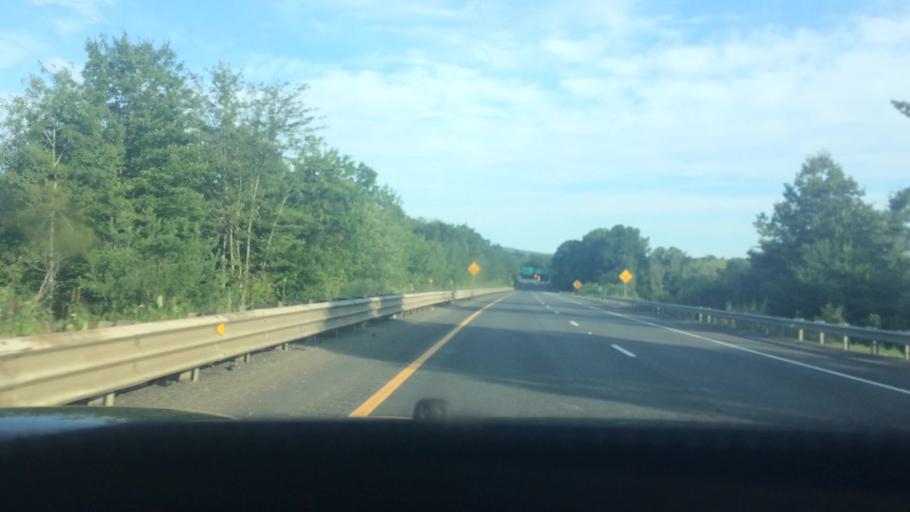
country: US
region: Massachusetts
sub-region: Franklin County
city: Greenfield
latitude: 42.6110
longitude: -72.5852
